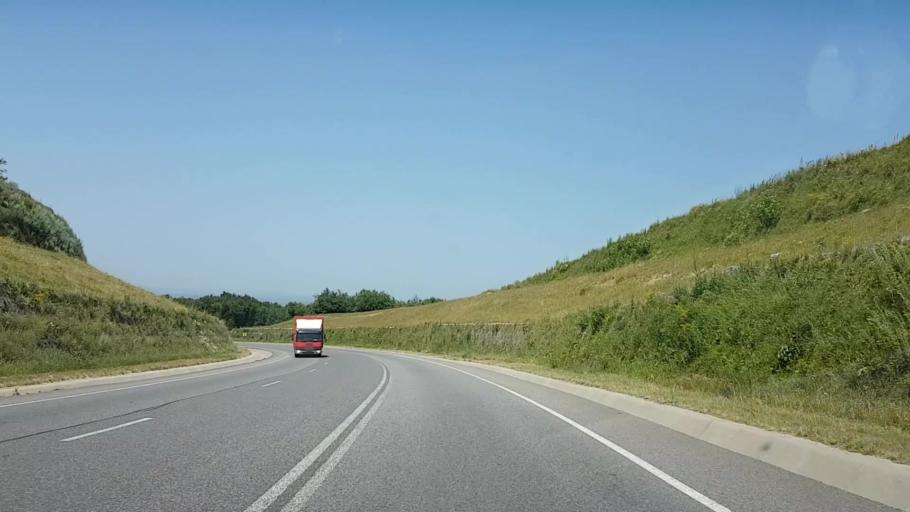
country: RO
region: Cluj
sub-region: Comuna Feleacu
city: Gheorghieni
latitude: 46.7135
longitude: 23.6623
